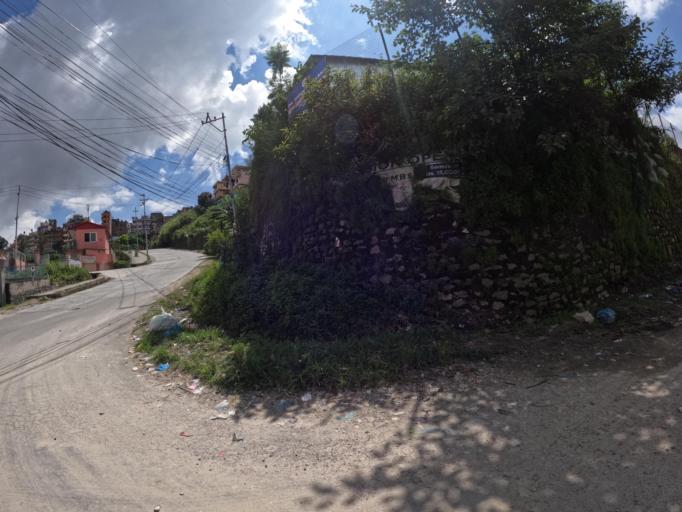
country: NP
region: Central Region
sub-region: Bagmati Zone
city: Kathmandu
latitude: 27.7708
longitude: 85.3294
